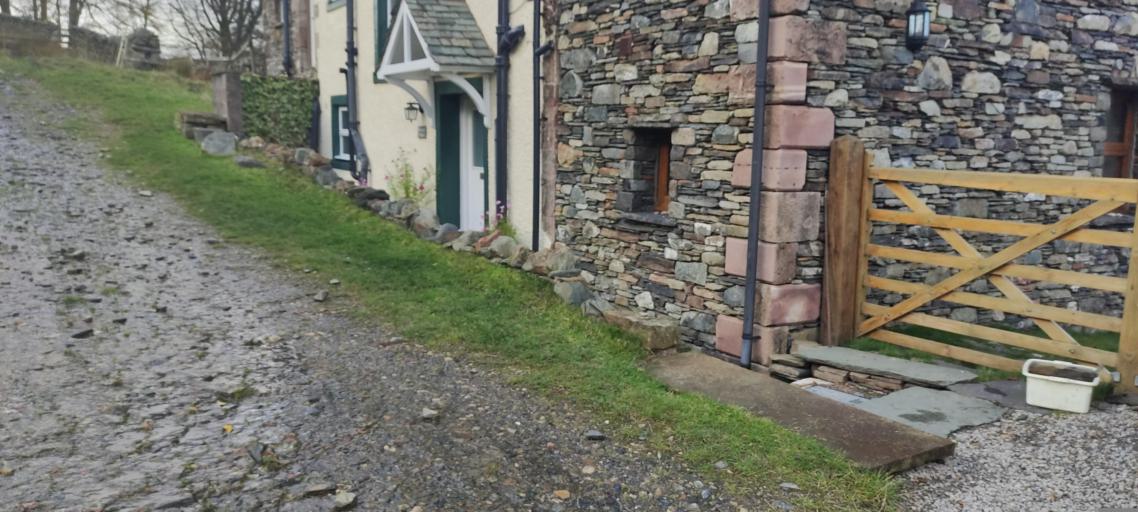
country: GB
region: England
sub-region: Cumbria
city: Keswick
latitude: 54.6761
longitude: -2.9969
